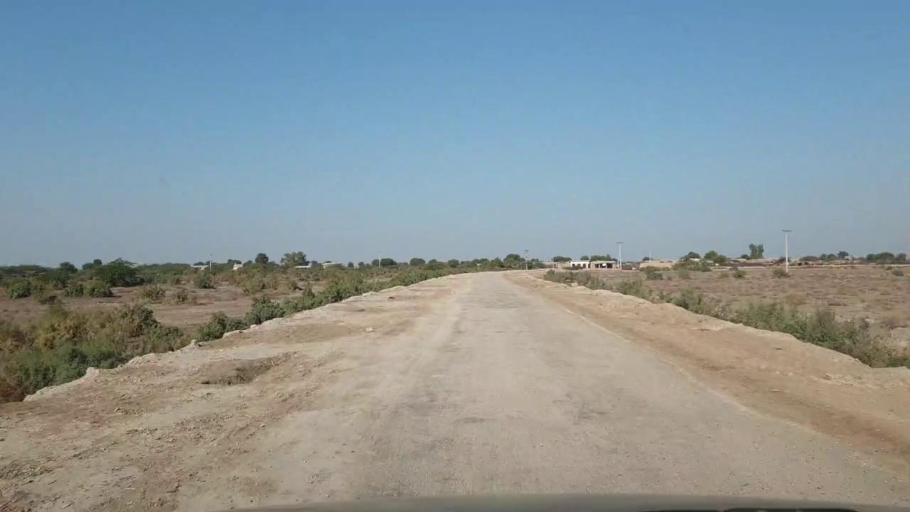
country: PK
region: Sindh
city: Shahpur Chakar
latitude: 26.1551
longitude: 68.6760
